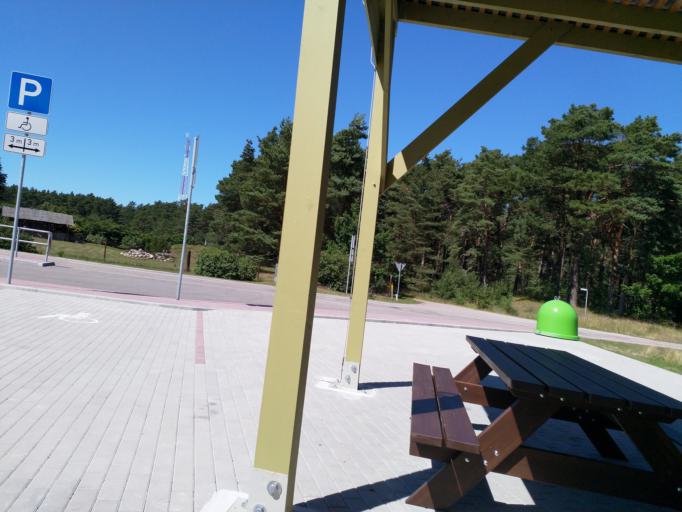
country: LV
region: Rojas
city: Roja
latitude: 57.7509
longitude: 22.5957
